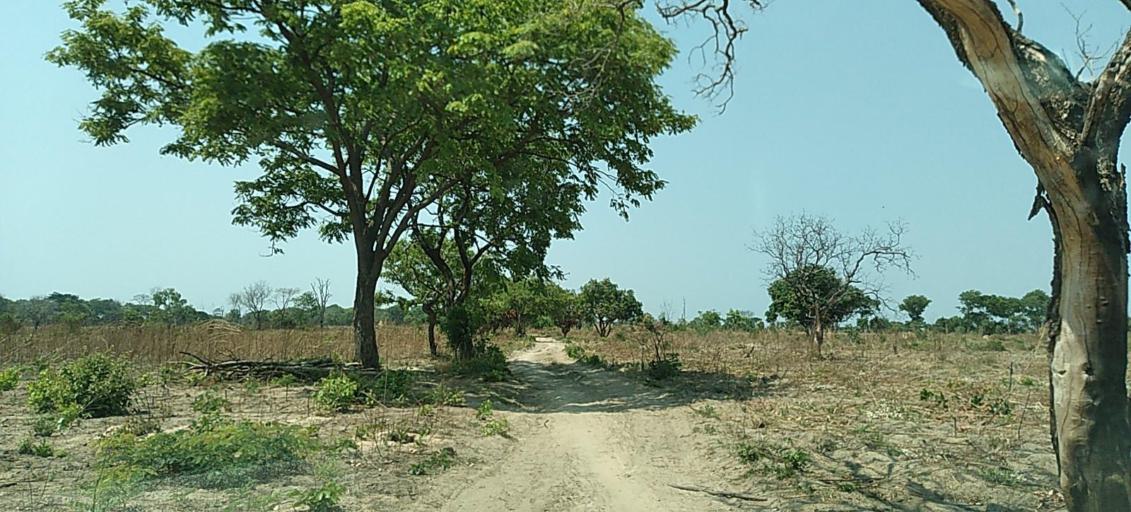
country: ZM
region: Copperbelt
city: Mpongwe
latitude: -13.8597
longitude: 28.0554
